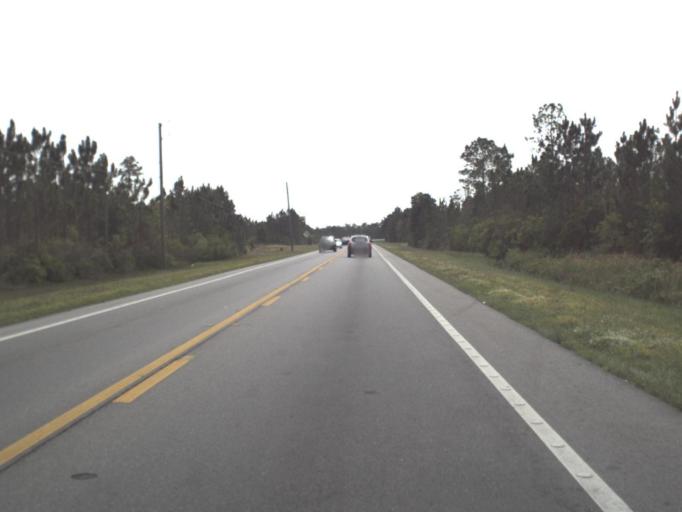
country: US
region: Florida
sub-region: Escambia County
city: Myrtle Grove
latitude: 30.3997
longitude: -87.3426
